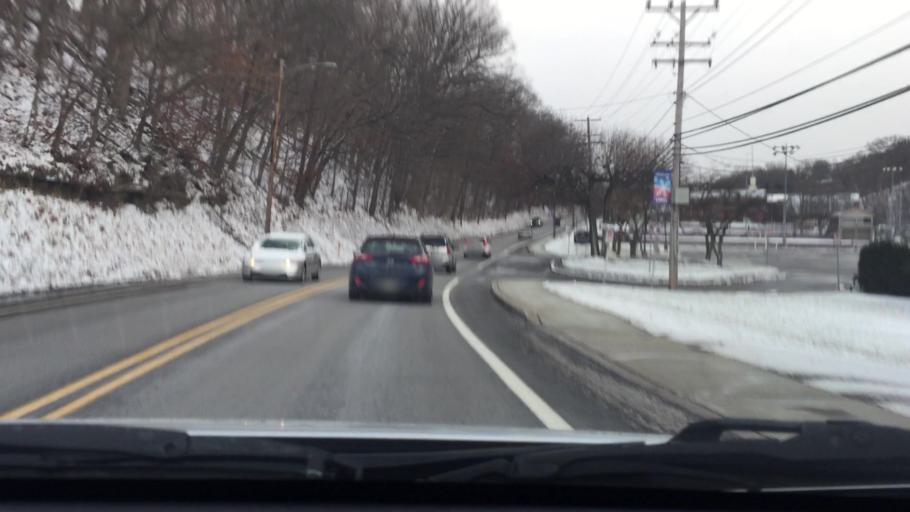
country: US
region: Pennsylvania
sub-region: Allegheny County
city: Upper Saint Clair
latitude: 40.3358
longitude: -80.0741
